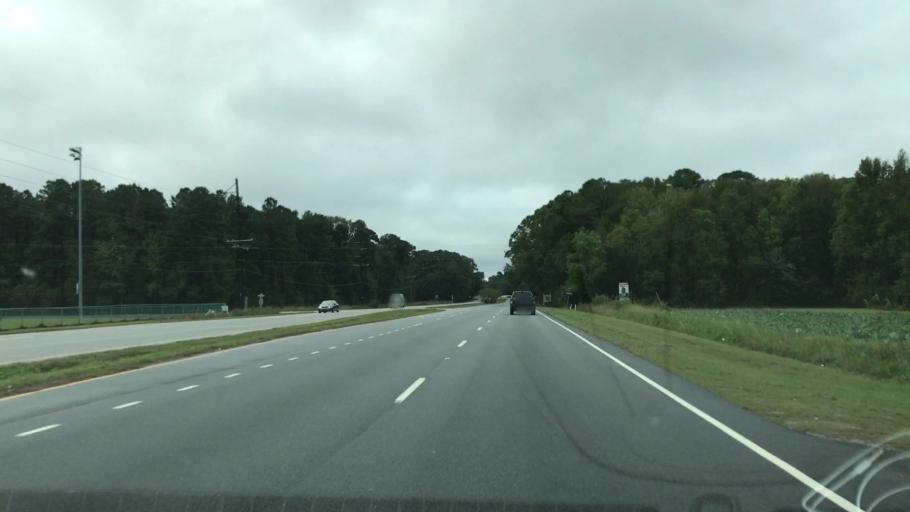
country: US
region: South Carolina
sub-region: Beaufort County
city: Laurel Bay
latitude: 32.5330
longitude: -80.7471
